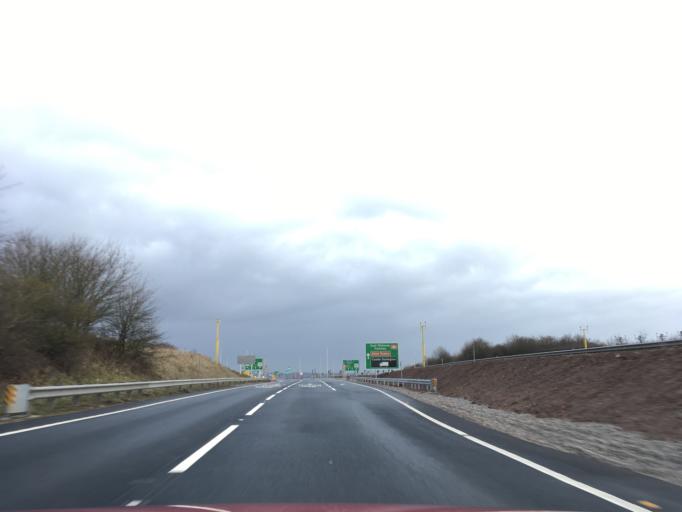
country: GB
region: England
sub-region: Leicestershire
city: Kegworth
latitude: 52.8307
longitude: -1.3012
